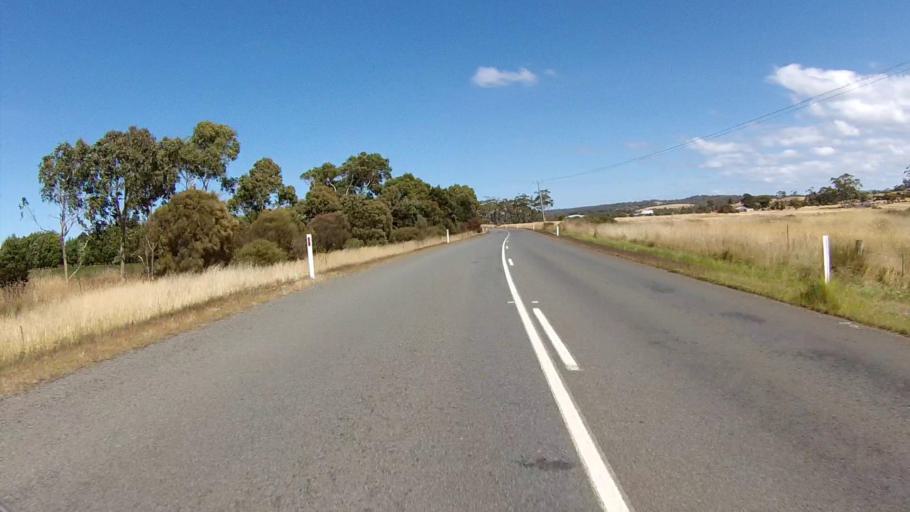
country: AU
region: Tasmania
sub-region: Break O'Day
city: St Helens
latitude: -42.1079
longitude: 148.0566
